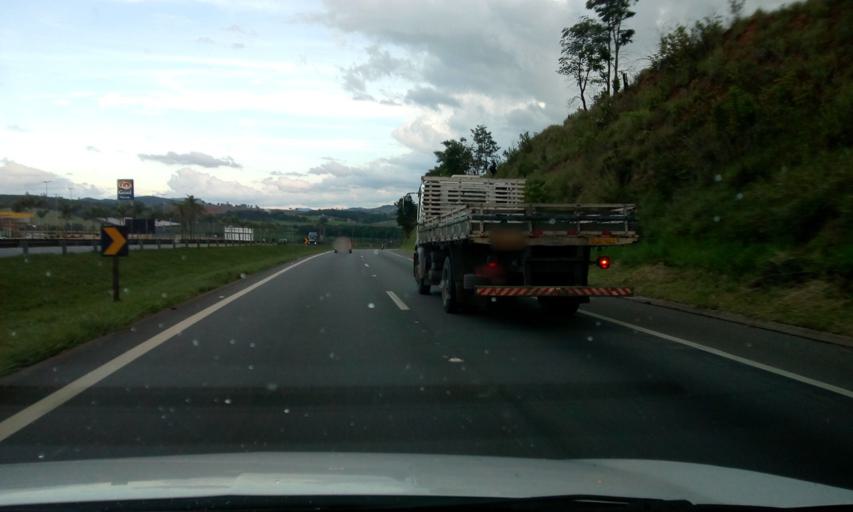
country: BR
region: Sao Paulo
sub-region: Jarinu
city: Jarinu
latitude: -23.0375
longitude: -46.6902
